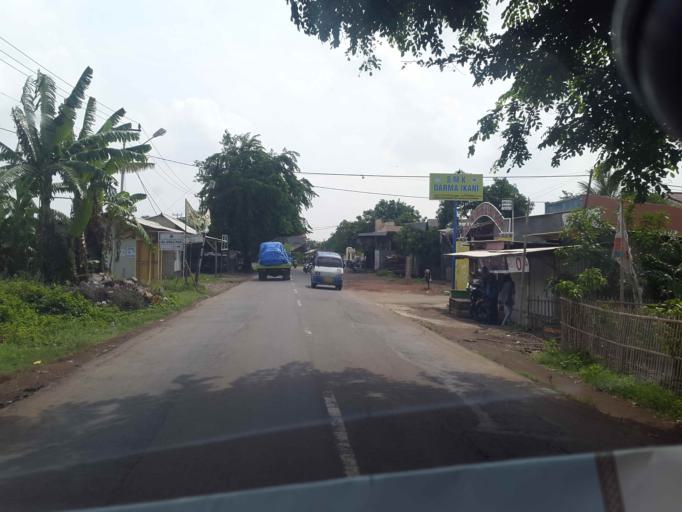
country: ID
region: West Java
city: Rengasdengklok
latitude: -6.2944
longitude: 107.3392
